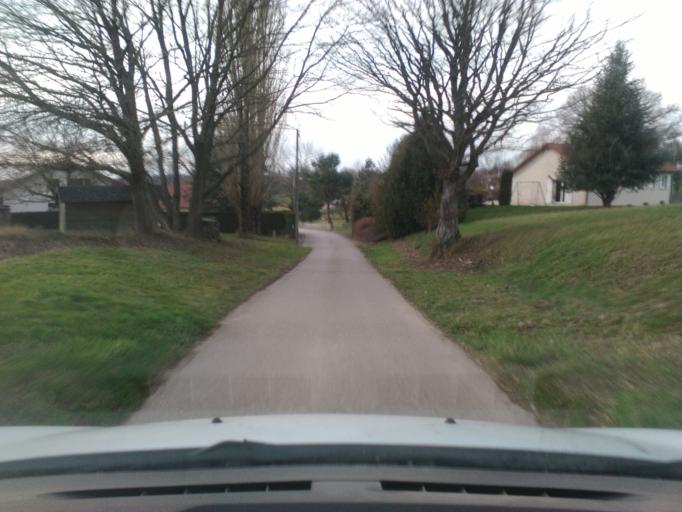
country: FR
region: Lorraine
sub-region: Departement des Vosges
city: Jeanmenil
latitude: 48.3302
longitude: 6.7060
